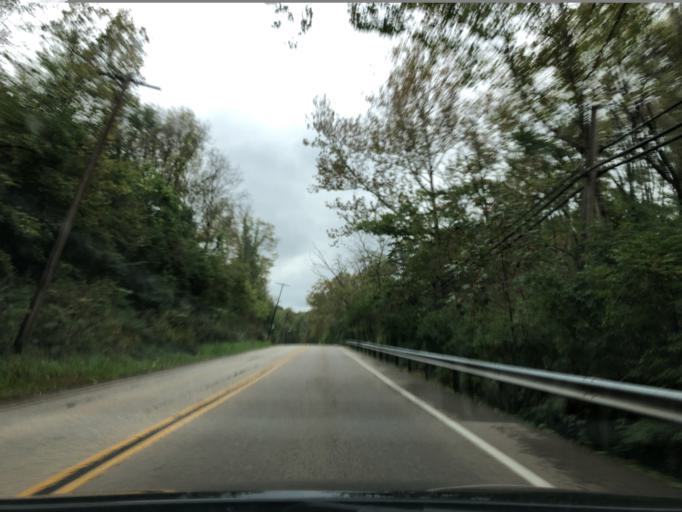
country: US
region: Ohio
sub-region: Hamilton County
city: Madeira
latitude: 39.1705
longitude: -84.3773
